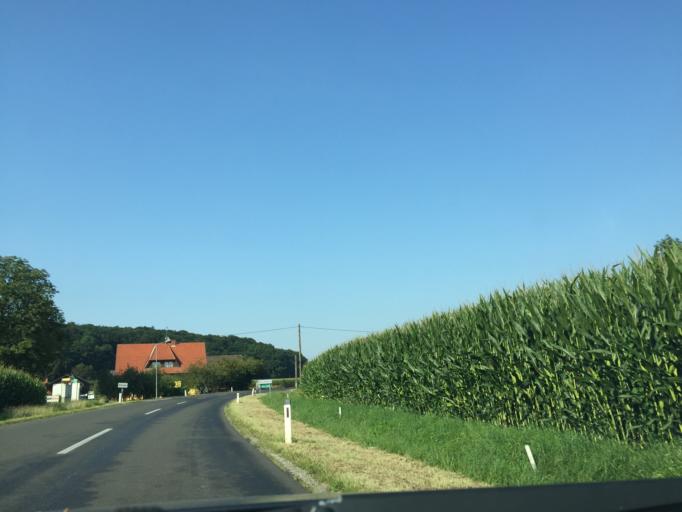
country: AT
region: Styria
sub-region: Politischer Bezirk Suedoststeiermark
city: Deutsch Goritz
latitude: 46.7590
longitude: 15.8405
